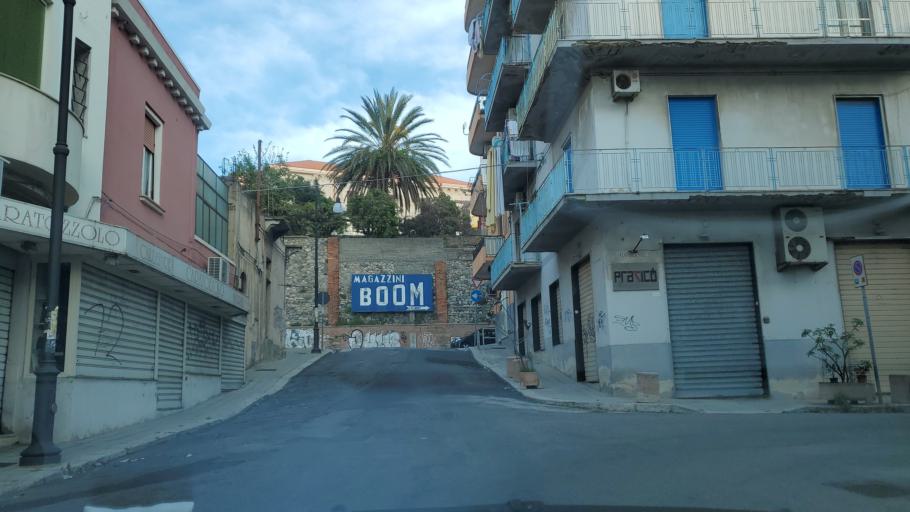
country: IT
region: Calabria
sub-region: Provincia di Reggio Calabria
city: Reggio Calabria
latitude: 38.1078
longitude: 15.6469
